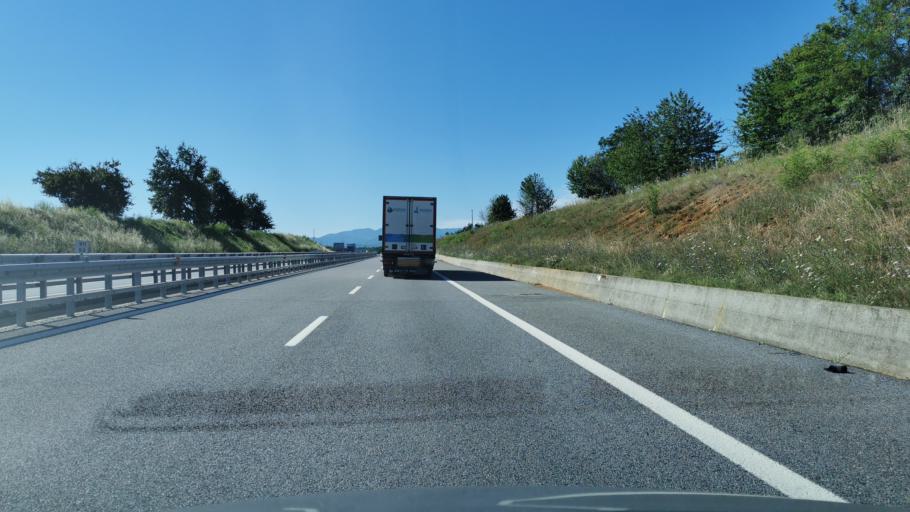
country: IT
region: Piedmont
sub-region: Provincia di Cuneo
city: Magliano Alpi
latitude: 44.4996
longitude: 7.8102
